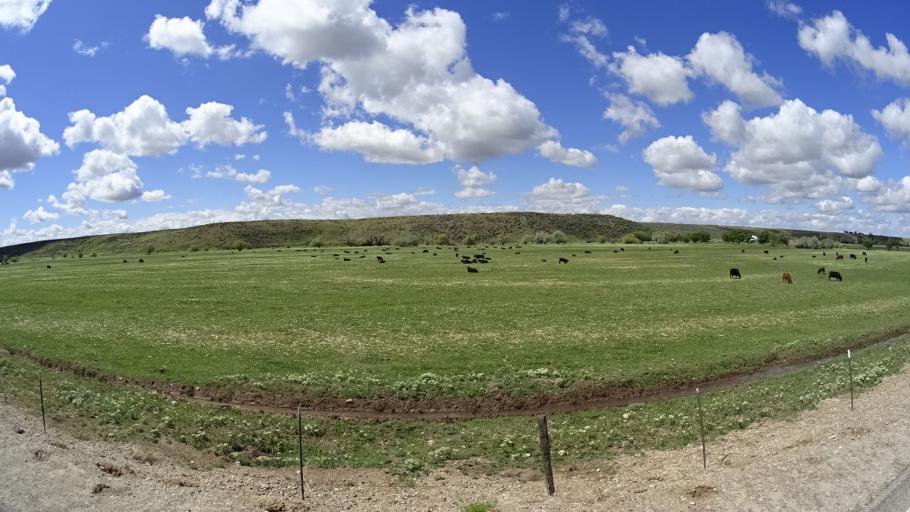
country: US
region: Idaho
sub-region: Ada County
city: Garden City
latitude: 43.4971
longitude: -116.2807
